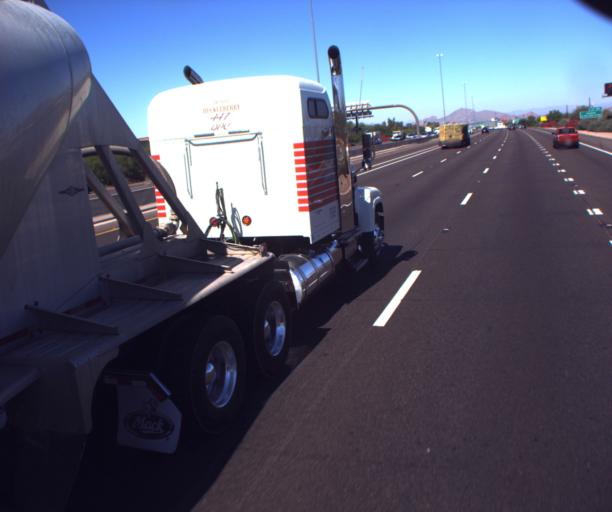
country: US
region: Arizona
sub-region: Maricopa County
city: Guadalupe
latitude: 33.3648
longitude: -111.9684
